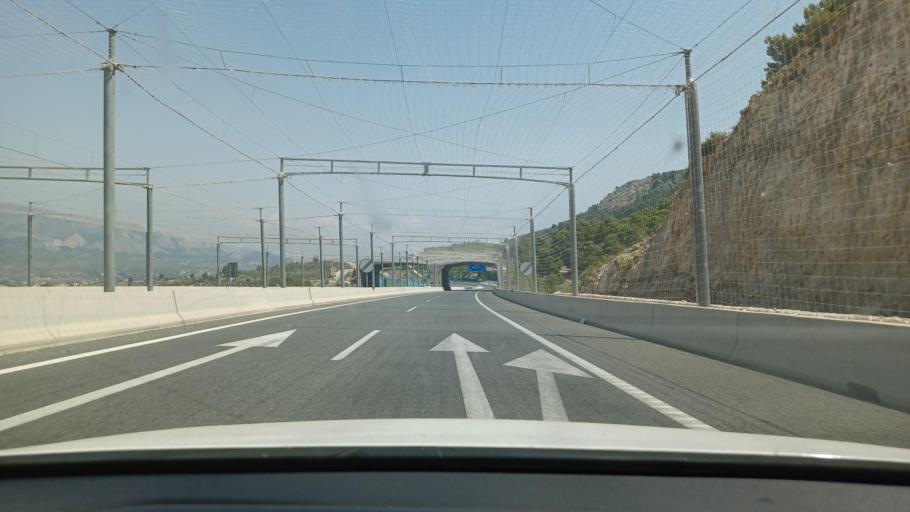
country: ES
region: Valencia
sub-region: Provincia de Alicante
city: Alcoy
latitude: 38.6774
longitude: -0.4639
